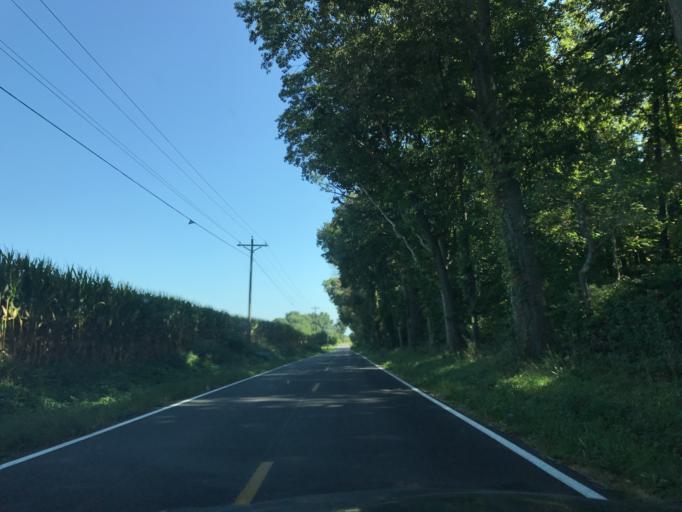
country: US
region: Maryland
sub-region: Queen Anne's County
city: Kingstown
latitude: 39.2759
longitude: -75.9286
